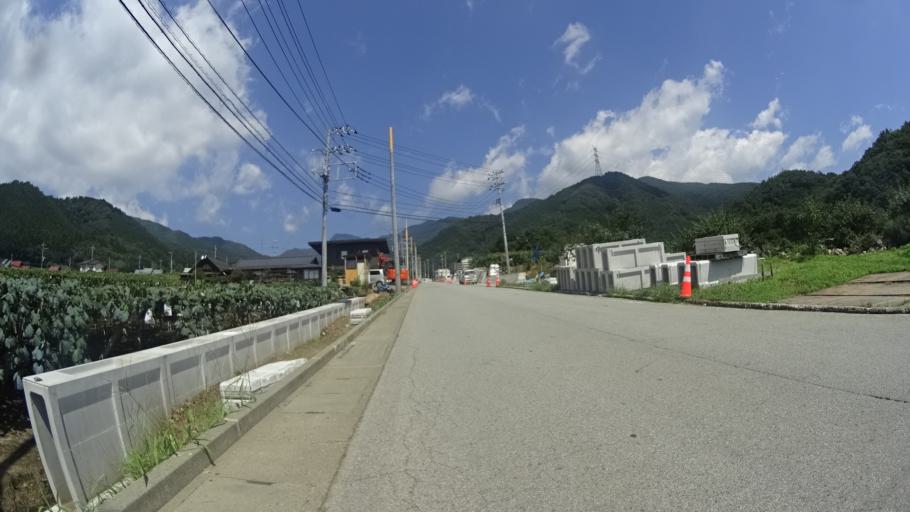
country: JP
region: Yamanashi
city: Enzan
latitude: 35.7662
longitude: 138.7042
